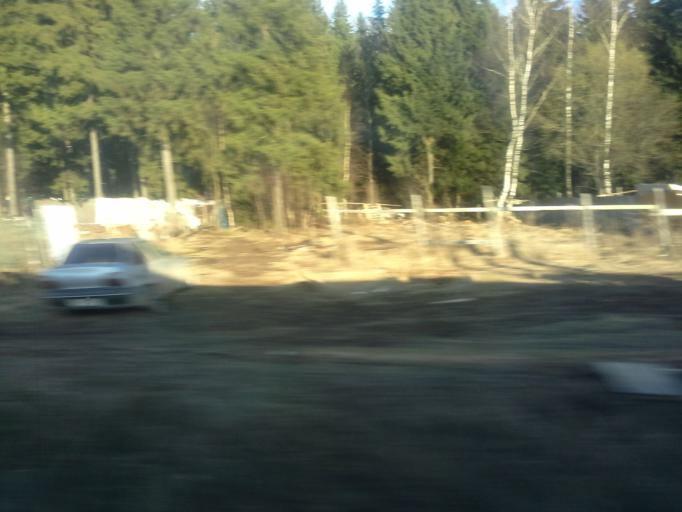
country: RU
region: Moskovskaya
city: Nekrasovskiy
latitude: 56.0987
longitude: 37.5085
